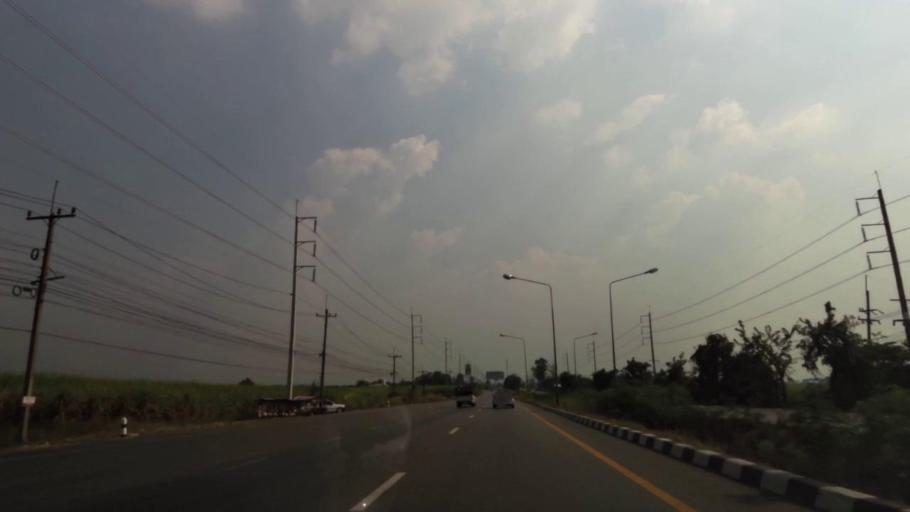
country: TH
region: Chon Buri
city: Nong Yai
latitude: 13.2148
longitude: 101.2401
